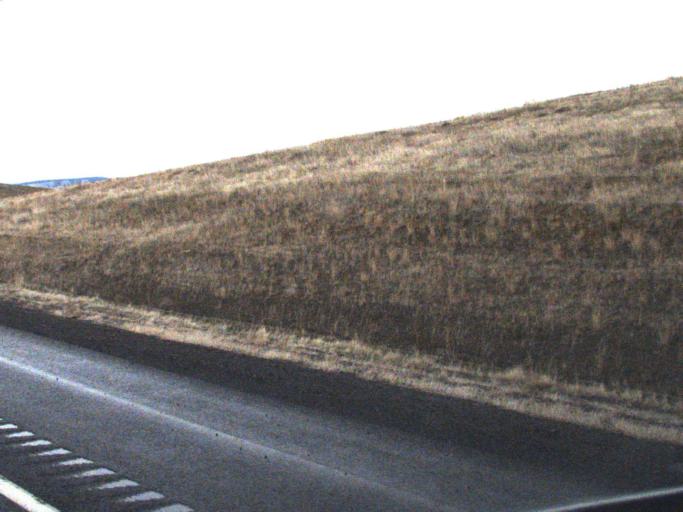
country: US
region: Washington
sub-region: Walla Walla County
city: Garrett
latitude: 46.0554
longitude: -118.4538
